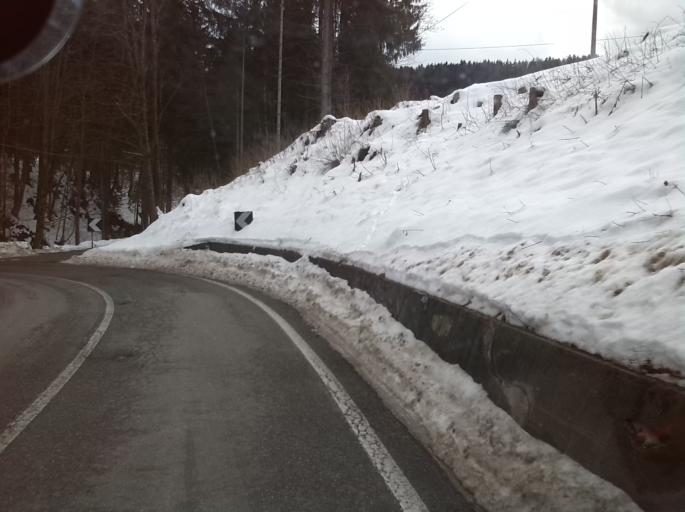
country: IT
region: Friuli Venezia Giulia
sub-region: Provincia di Udine
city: Tarvisio
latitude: 46.5046
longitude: 13.6154
